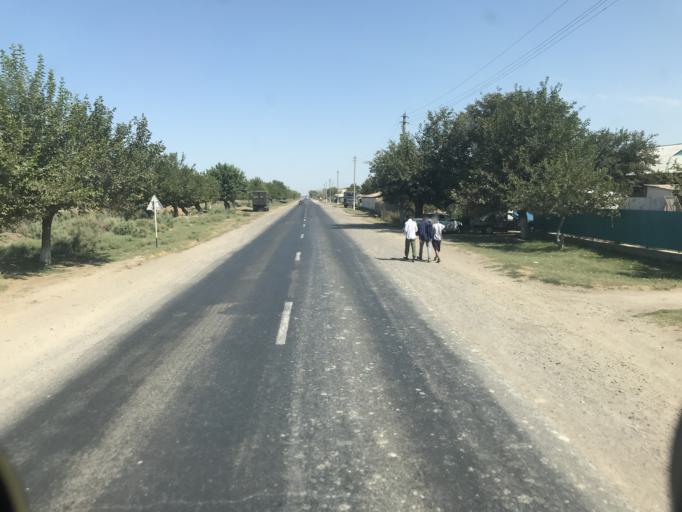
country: KZ
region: Ongtustik Qazaqstan
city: Ilyich
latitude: 40.7606
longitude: 68.5371
